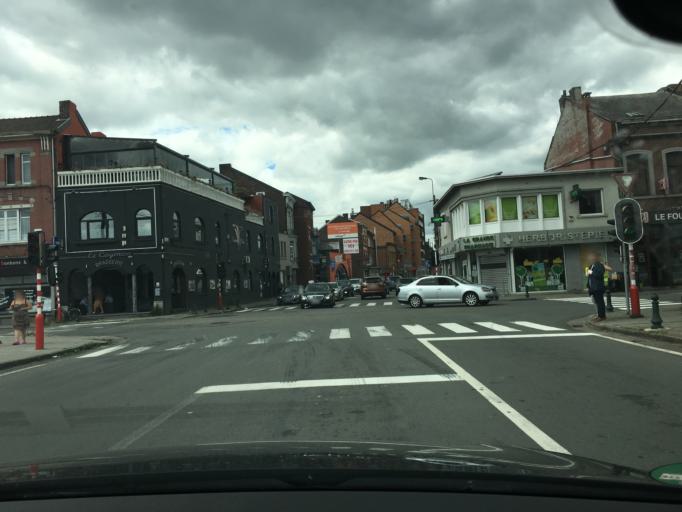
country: BE
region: Wallonia
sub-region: Province de Liege
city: Seraing
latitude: 50.6146
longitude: 5.5013
